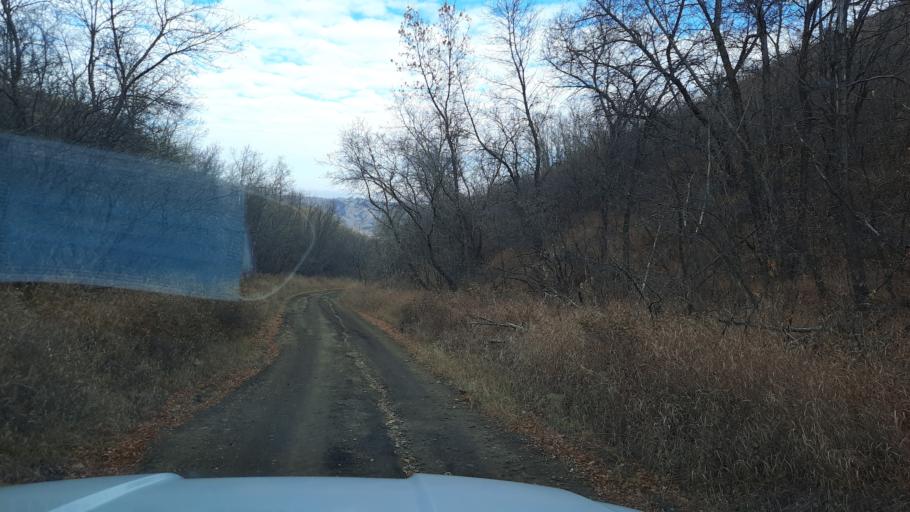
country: CA
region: Saskatchewan
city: Pilot Butte
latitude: 50.7766
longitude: -104.2112
